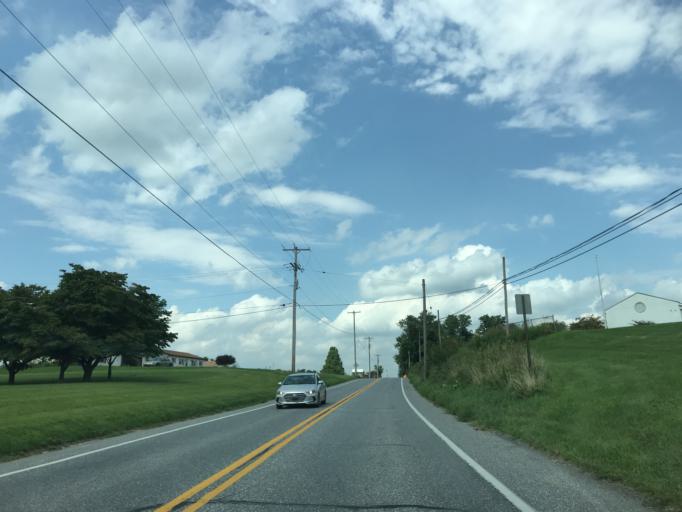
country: US
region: Pennsylvania
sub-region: York County
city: Red Lion
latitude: 39.8389
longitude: -76.6196
